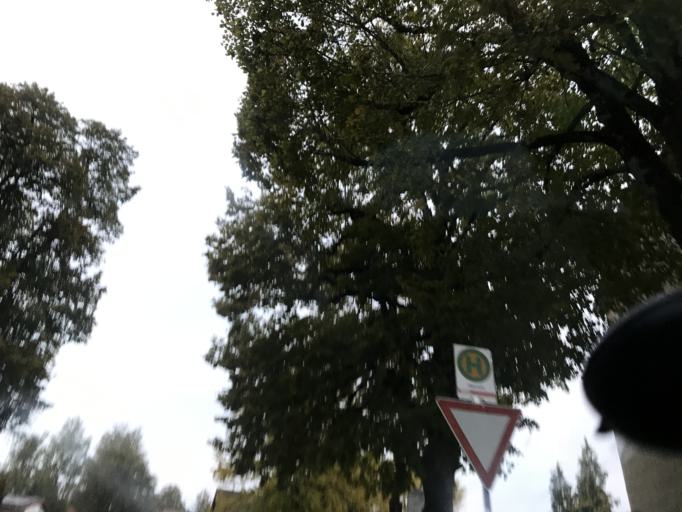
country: DE
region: Baden-Wuerttemberg
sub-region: Freiburg Region
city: Gorwihl
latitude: 47.6208
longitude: 8.0471
